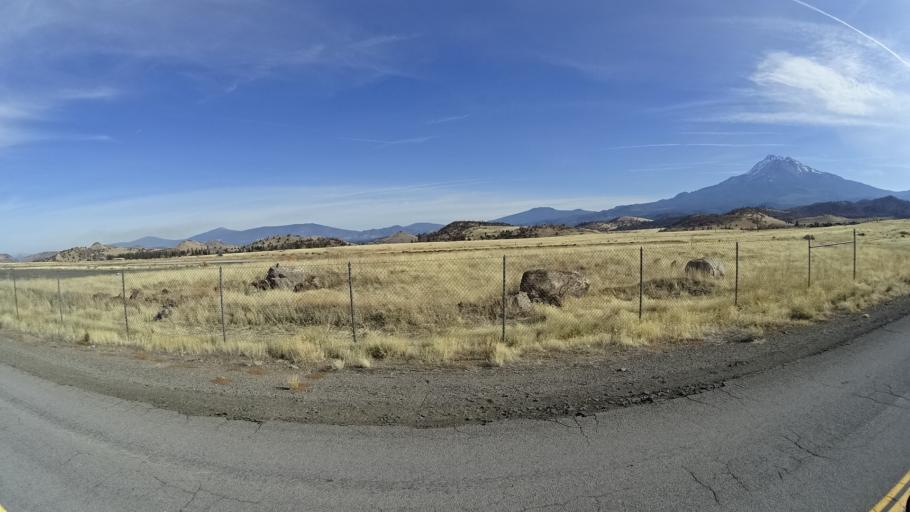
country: US
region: California
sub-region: Siskiyou County
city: Weed
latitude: 41.4739
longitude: -122.4520
